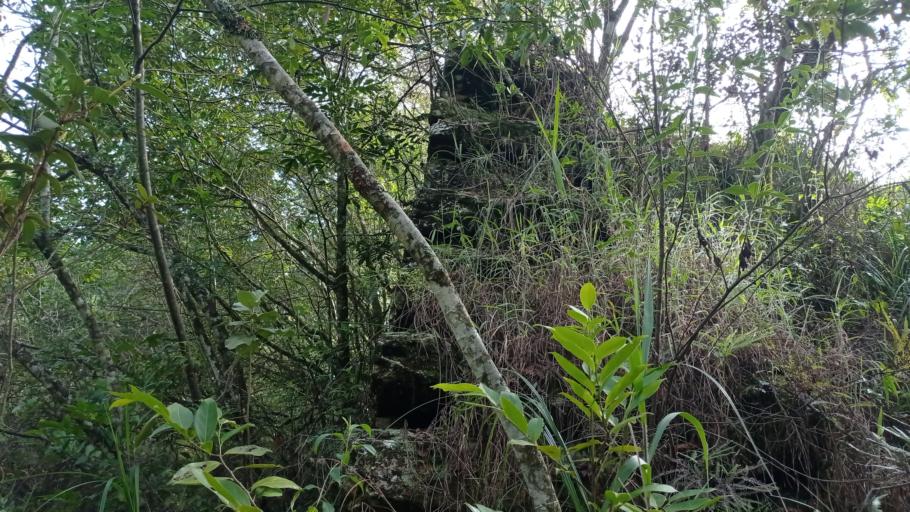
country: BR
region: Minas Gerais
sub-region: Sao Joao Del Rei
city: Sao Joao del Rei
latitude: -21.1394
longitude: -44.2889
